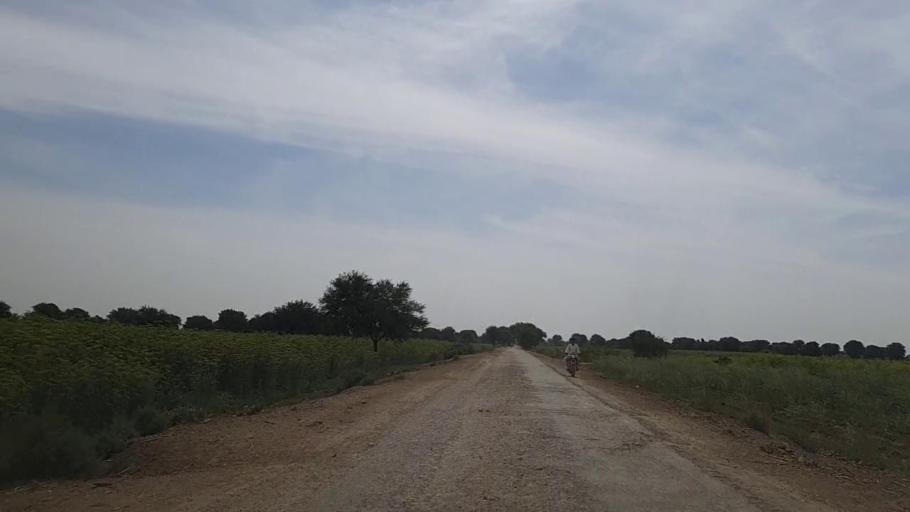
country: PK
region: Sindh
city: Samaro
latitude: 25.2840
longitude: 69.4537
